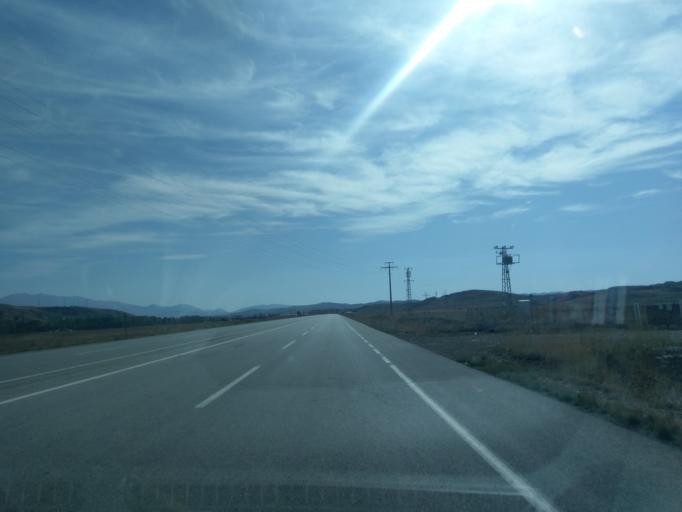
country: TR
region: Sivas
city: Imranli
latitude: 39.8740
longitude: 38.0852
